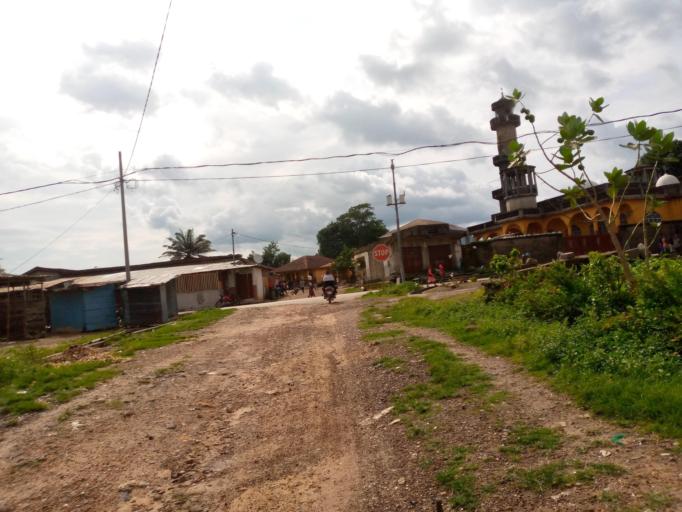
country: SL
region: Northern Province
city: Magburaka
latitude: 8.7246
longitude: -11.9482
